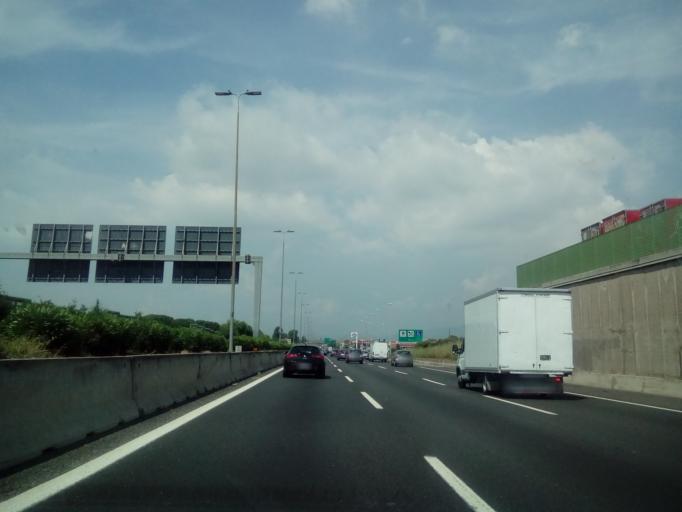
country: IT
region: Latium
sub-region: Citta metropolitana di Roma Capitale
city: Ciampino
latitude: 41.8715
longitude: 12.6050
